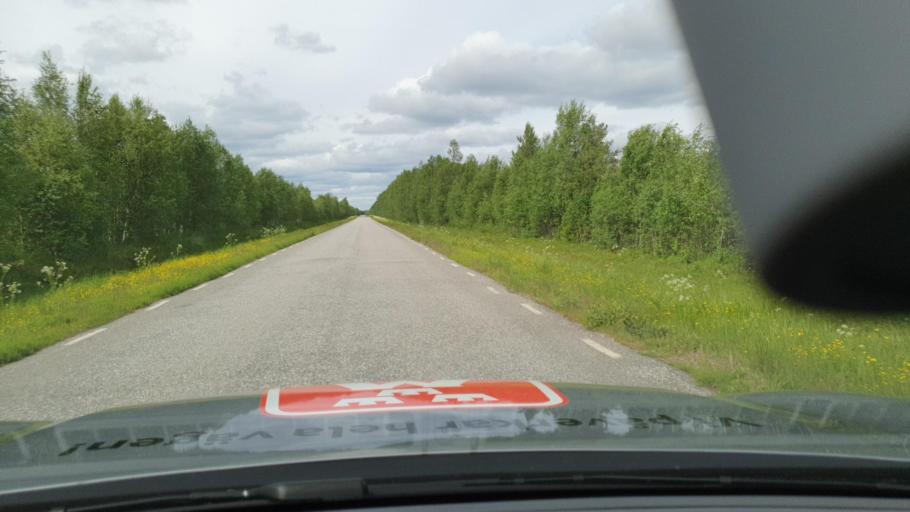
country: FI
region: Lapland
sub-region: Torniolaakso
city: Ylitornio
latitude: 66.0380
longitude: 23.7680
